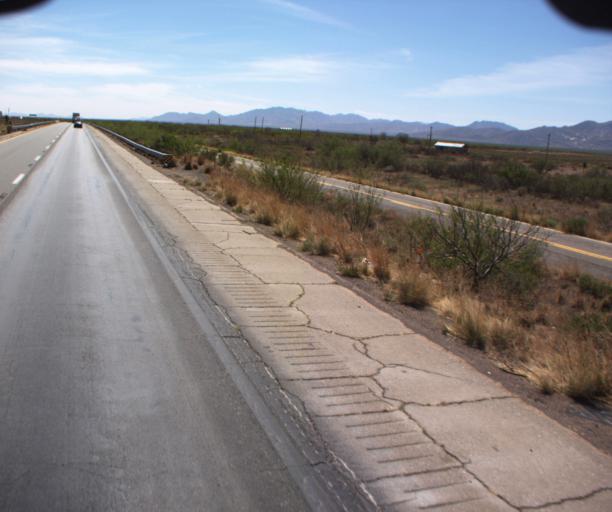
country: US
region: Arizona
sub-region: Cochise County
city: Willcox
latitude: 32.3234
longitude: -109.5037
